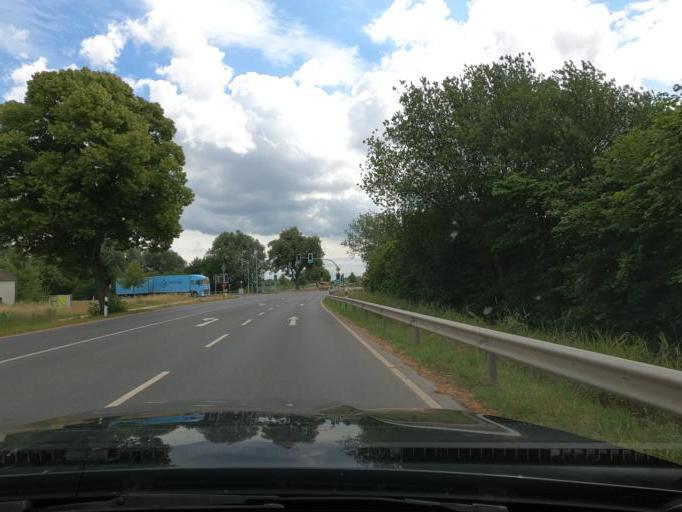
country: DE
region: Lower Saxony
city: Sehnde
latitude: 52.3320
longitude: 9.9483
